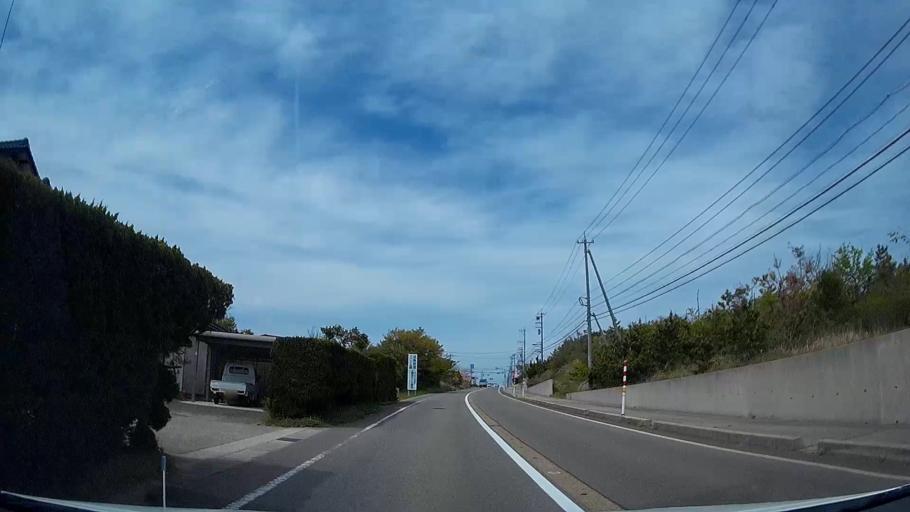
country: JP
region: Ishikawa
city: Hakui
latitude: 36.9860
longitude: 136.7756
